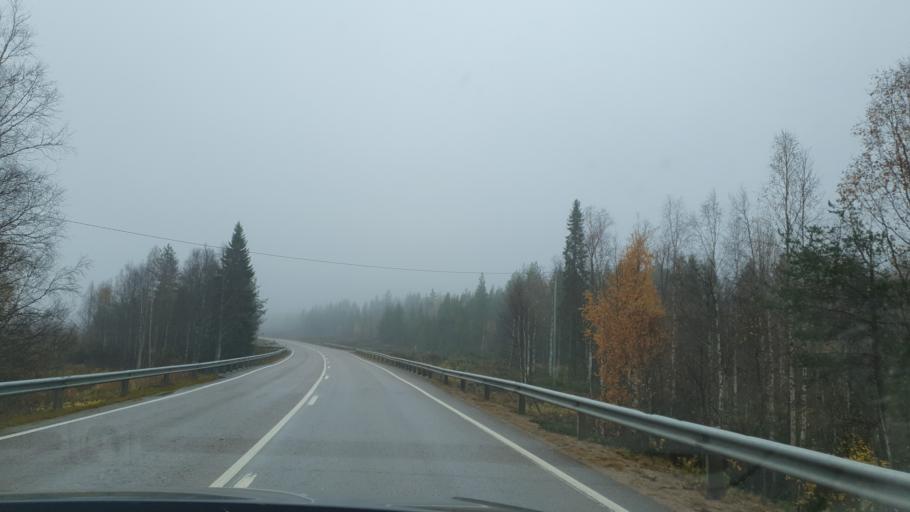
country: FI
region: Lapland
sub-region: Rovaniemi
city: Rovaniemi
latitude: 66.8153
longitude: 25.3970
